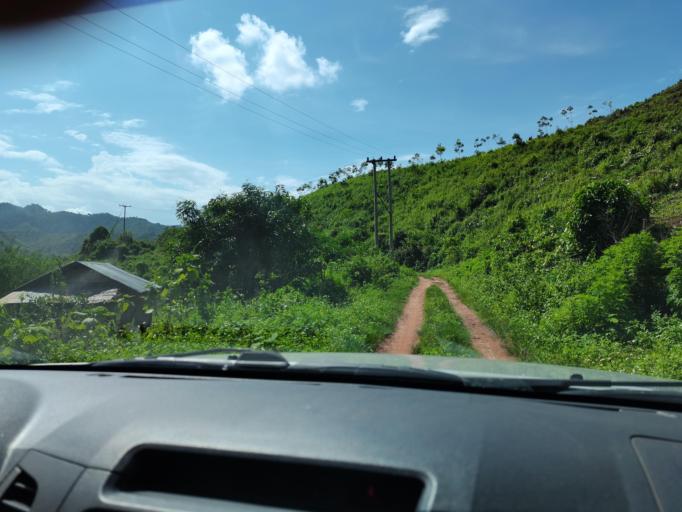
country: LA
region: Loungnamtha
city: Muang Nale
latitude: 20.5551
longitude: 101.0652
